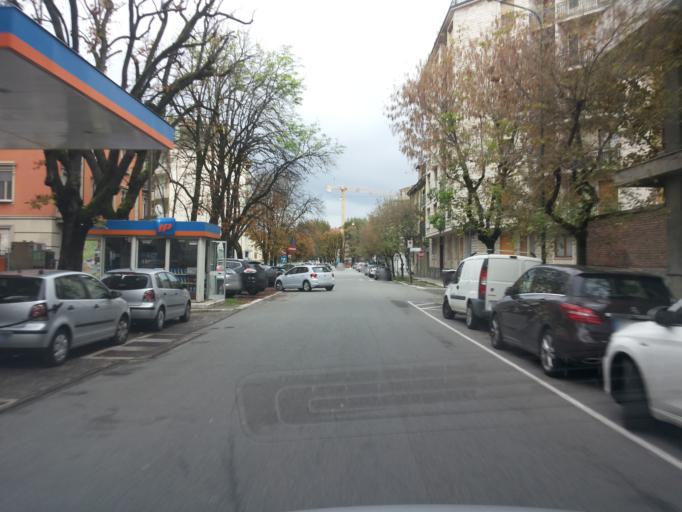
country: IT
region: Piedmont
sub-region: Provincia di Alessandria
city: Casale Monferrato
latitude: 45.1334
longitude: 8.4480
